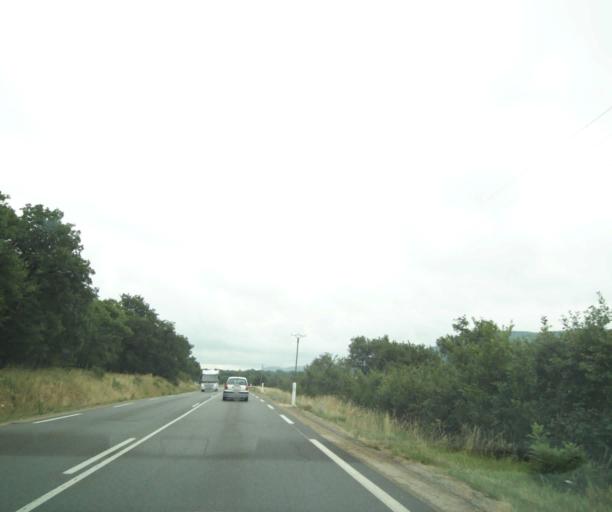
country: FR
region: Midi-Pyrenees
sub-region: Departement de l'Aveyron
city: Laissac
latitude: 44.3646
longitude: 2.8748
